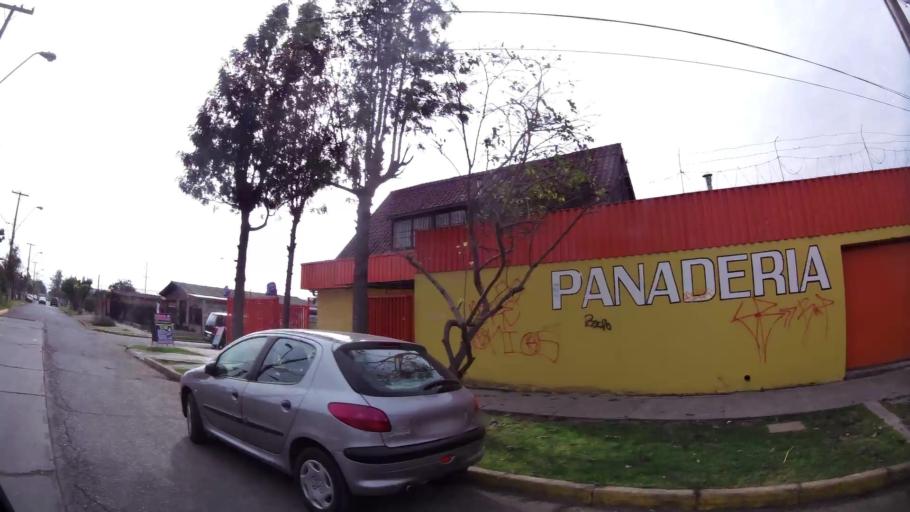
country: CL
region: Santiago Metropolitan
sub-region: Provincia de Santiago
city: Lo Prado
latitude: -33.5195
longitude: -70.7666
